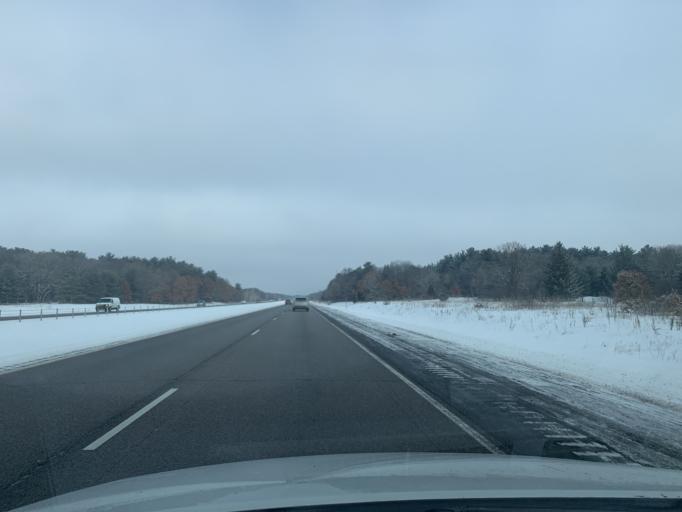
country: US
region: Minnesota
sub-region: Chisago County
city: Wyoming
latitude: 45.3637
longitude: -92.9962
